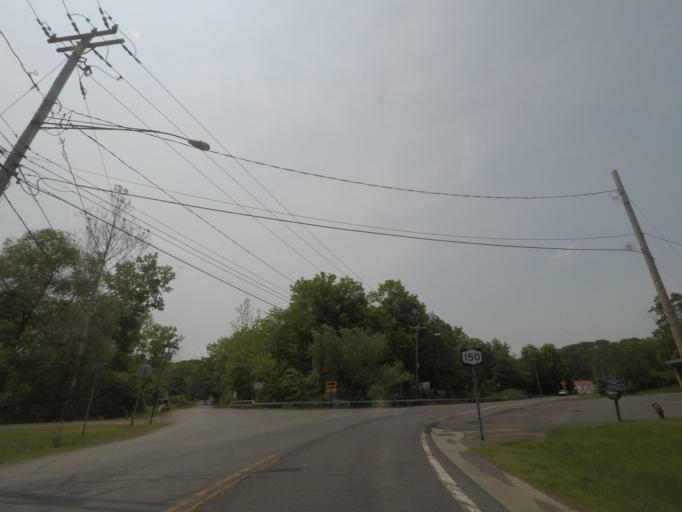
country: US
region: New York
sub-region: Rensselaer County
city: East Greenbush
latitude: 42.5498
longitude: -73.6889
